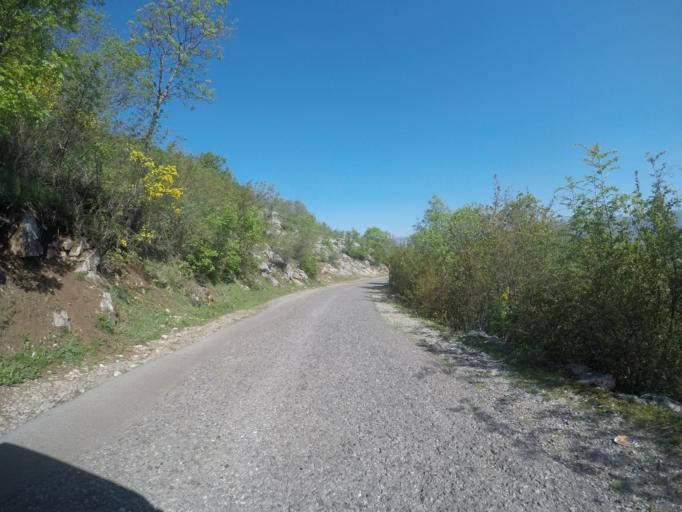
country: ME
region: Danilovgrad
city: Danilovgrad
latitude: 42.5266
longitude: 19.0942
